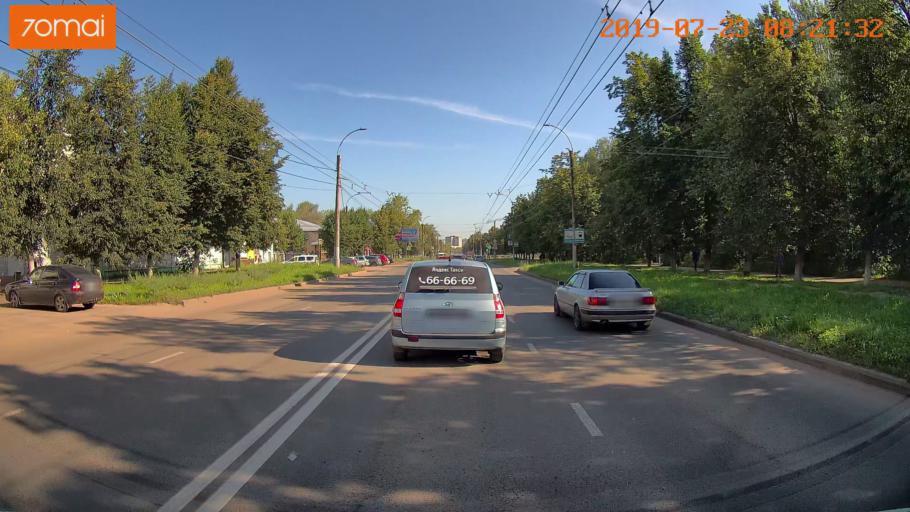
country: RU
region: Ivanovo
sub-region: Gorod Ivanovo
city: Ivanovo
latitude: 56.9754
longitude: 40.9655
